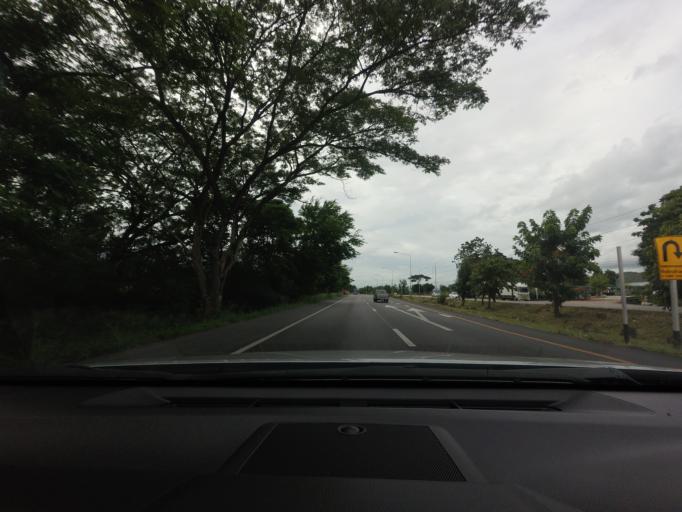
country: TH
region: Prachuap Khiri Khan
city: Hua Hin
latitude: 12.5963
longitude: 99.8632
